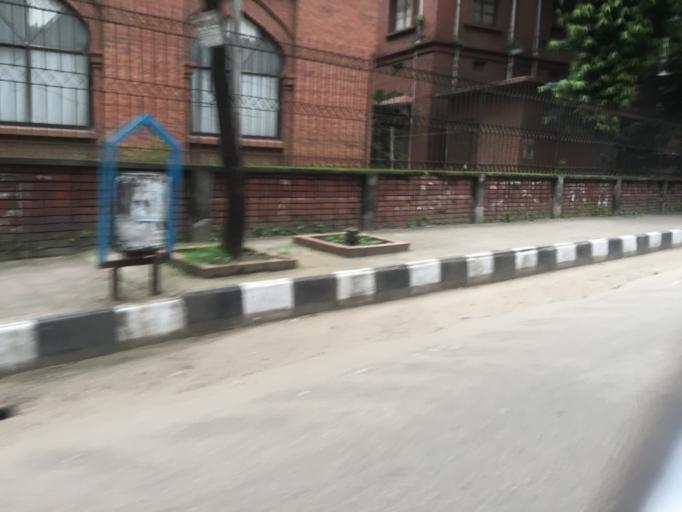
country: BD
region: Dhaka
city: Paltan
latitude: 23.7266
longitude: 90.4042
